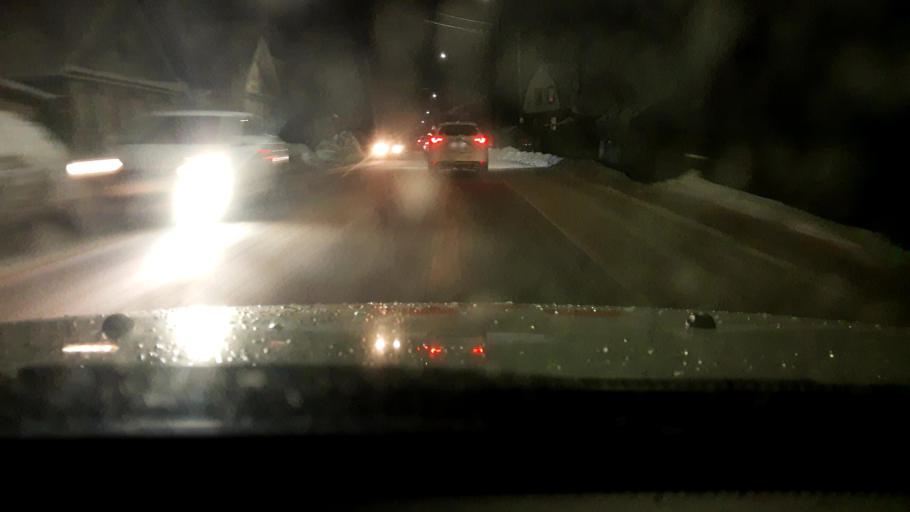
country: RU
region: Nizjnij Novgorod
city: Gorodets
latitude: 56.6596
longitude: 43.4705
